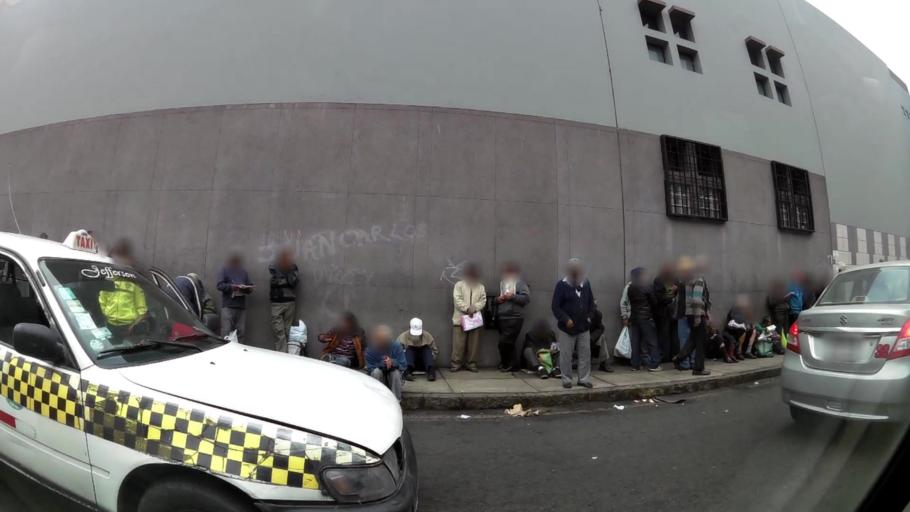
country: PE
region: Lima
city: Lima
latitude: -12.0455
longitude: -77.0382
